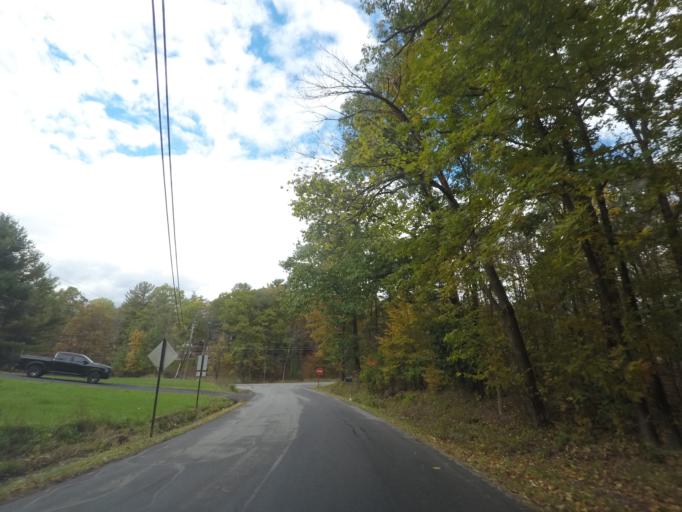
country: US
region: New York
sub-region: Rensselaer County
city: East Greenbush
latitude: 42.5808
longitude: -73.6647
